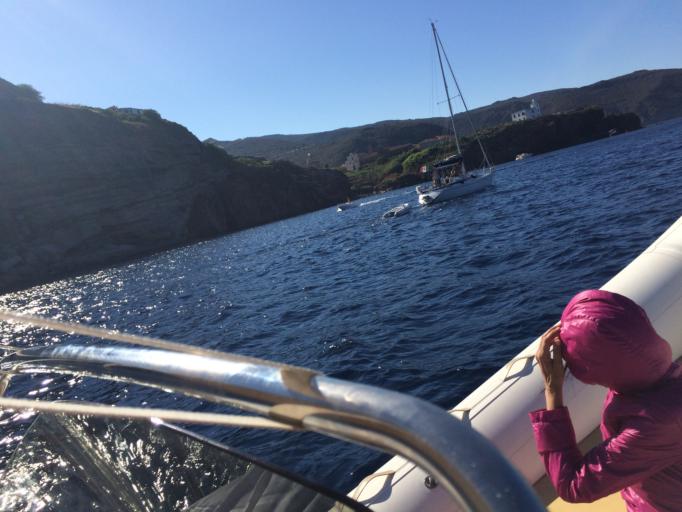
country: IT
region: Tuscany
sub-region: Provincia di Livorno
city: Capraia Isola
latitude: 43.0484
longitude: 9.8479
